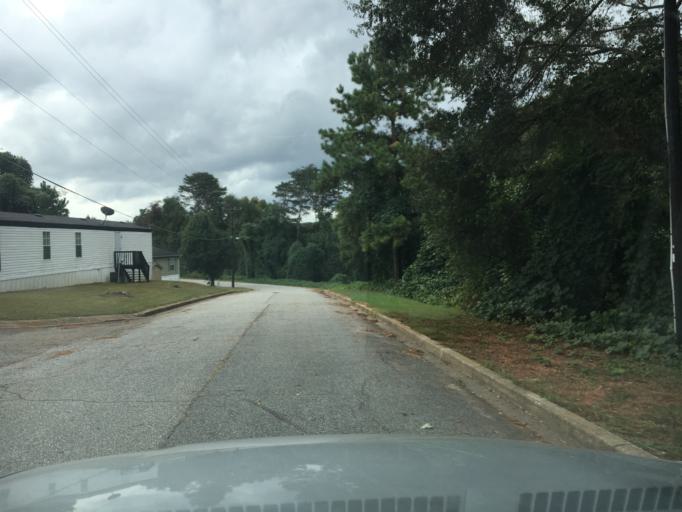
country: US
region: South Carolina
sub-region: Spartanburg County
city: Duncan
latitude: 34.9272
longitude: -82.1380
